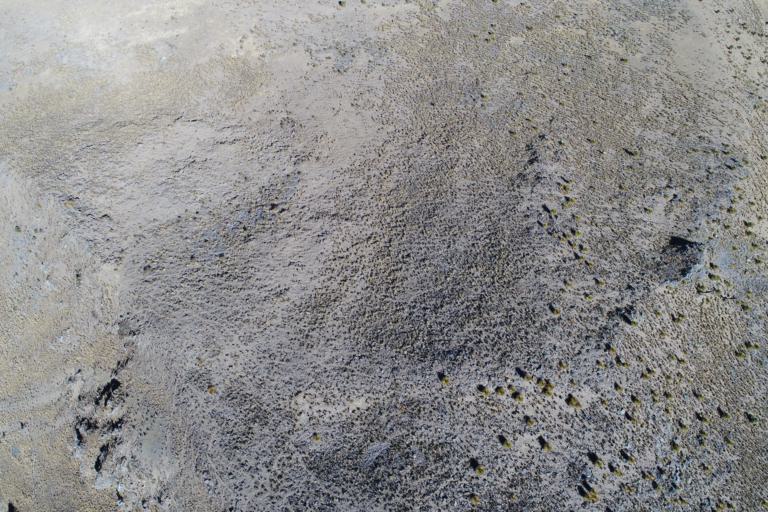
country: BO
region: La Paz
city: Viloco
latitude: -16.8121
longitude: -67.5459
